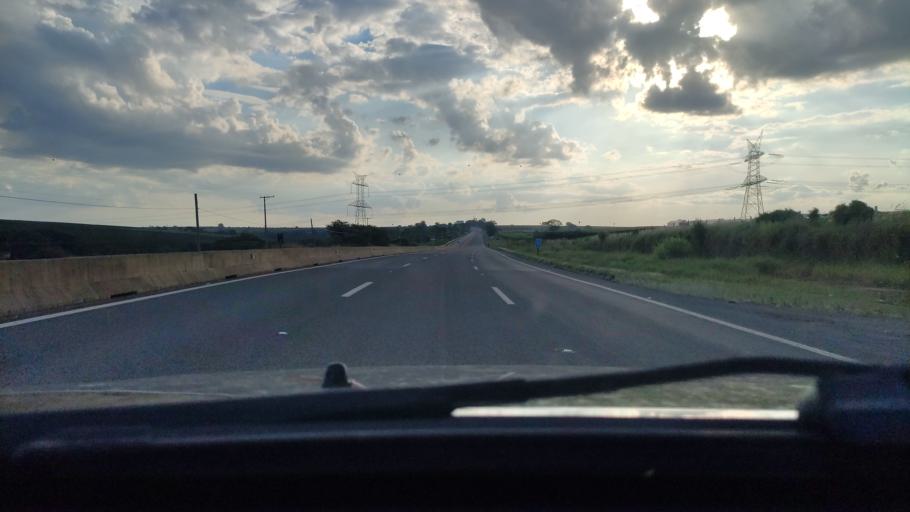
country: BR
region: Sao Paulo
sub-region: Mogi-Mirim
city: Mogi Mirim
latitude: -22.4502
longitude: -47.0631
